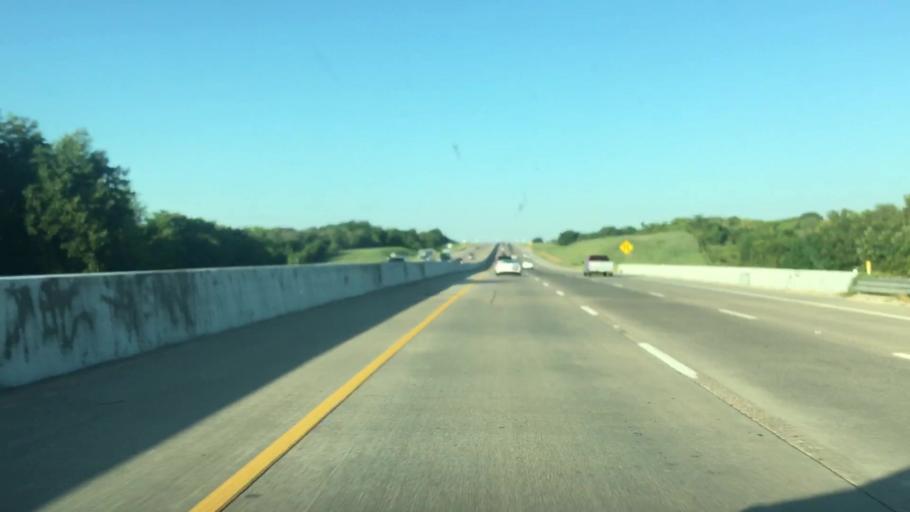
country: US
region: Texas
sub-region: Ellis County
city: Plum Grove
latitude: 32.1213
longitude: -96.9786
